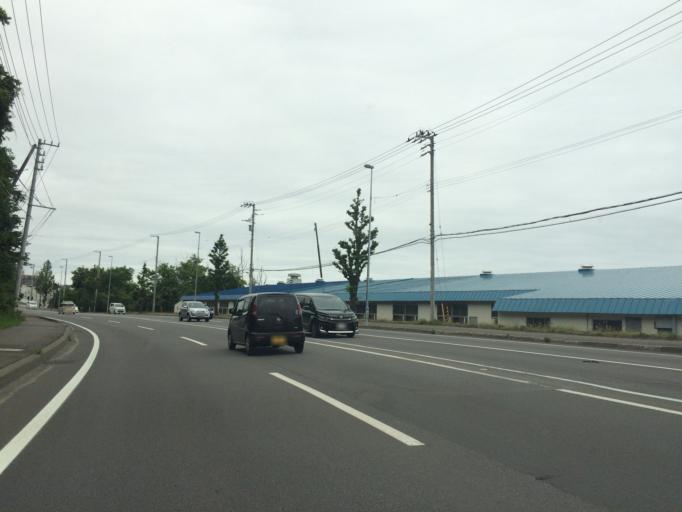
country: JP
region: Hokkaido
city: Otaru
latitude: 43.1378
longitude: 141.1688
